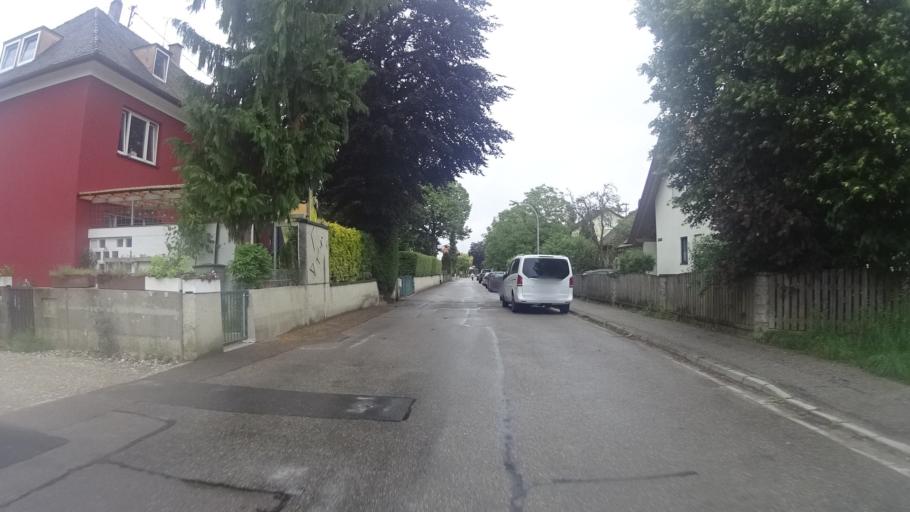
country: DE
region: Bavaria
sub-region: Upper Bavaria
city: Mammendorf
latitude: 48.2111
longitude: 11.1651
